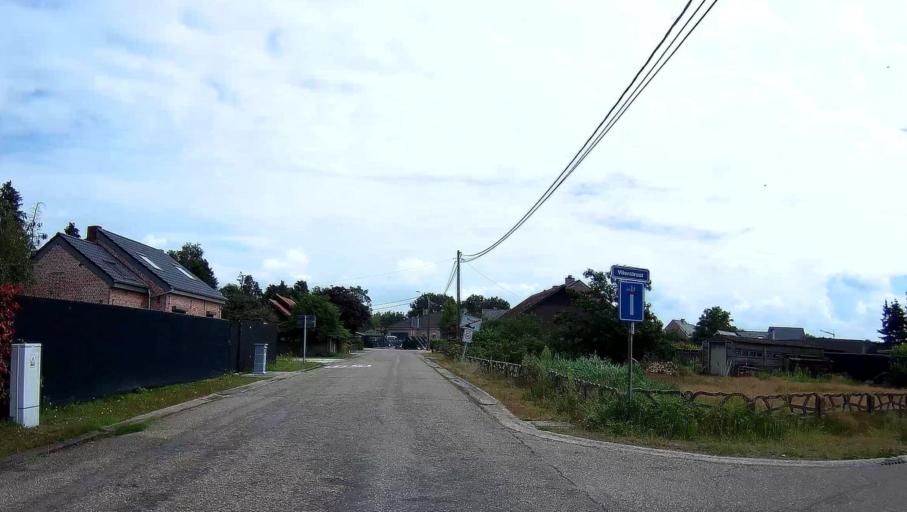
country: BE
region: Flanders
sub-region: Provincie Limburg
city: Leopoldsburg
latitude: 51.1906
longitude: 5.2418
